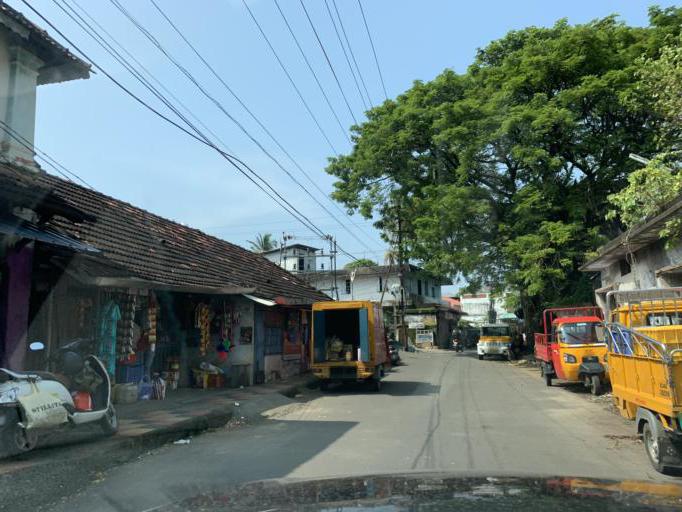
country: IN
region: Kerala
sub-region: Ernakulam
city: Cochin
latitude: 9.9476
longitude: 76.2608
